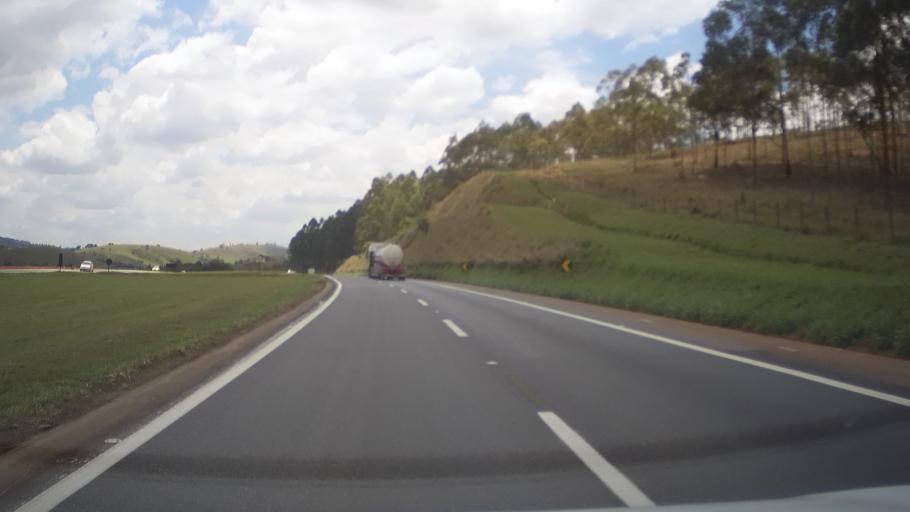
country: BR
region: Minas Gerais
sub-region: Campanha
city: Campanha
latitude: -21.7230
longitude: -45.3804
